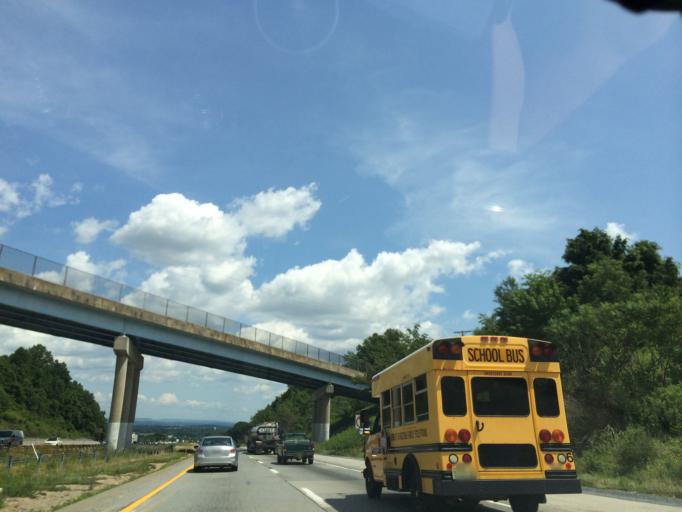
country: US
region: Pennsylvania
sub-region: Northampton County
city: Old Orchard
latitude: 40.6237
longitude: -75.2829
